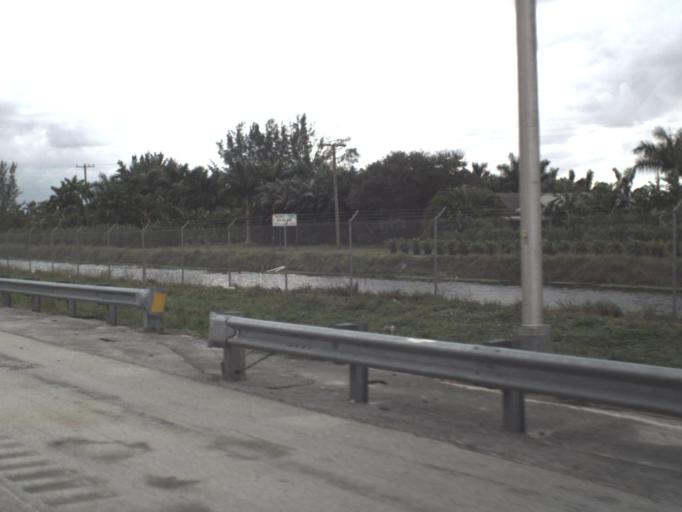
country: US
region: Florida
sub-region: Palm Beach County
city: Villages of Oriole
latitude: 26.5350
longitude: -80.1728
